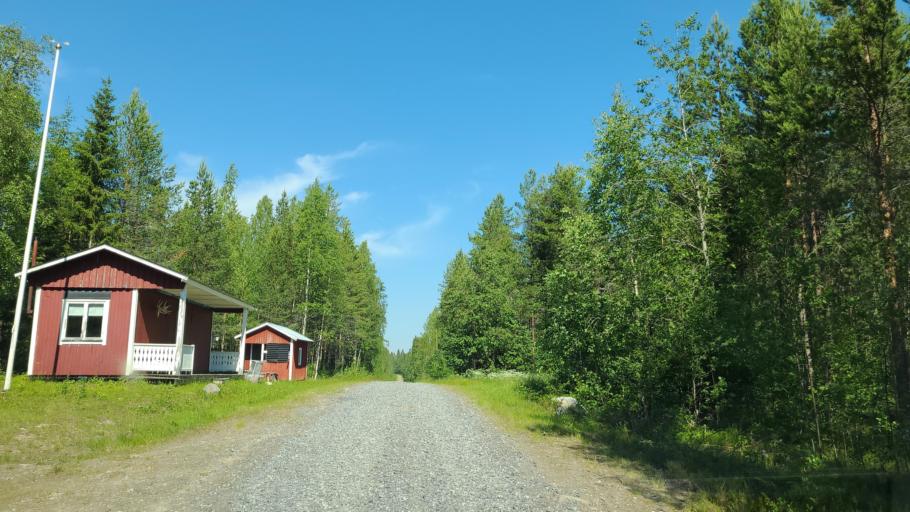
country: SE
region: Vaesterbotten
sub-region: Robertsfors Kommun
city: Robertsfors
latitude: 64.0957
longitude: 20.8343
